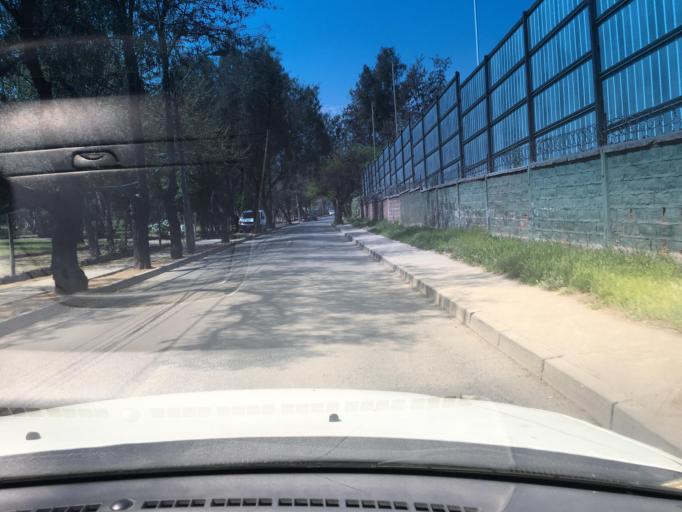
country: CL
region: Santiago Metropolitan
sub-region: Provincia de Santiago
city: Villa Presidente Frei, Nunoa, Santiago, Chile
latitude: -33.5143
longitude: -70.5476
